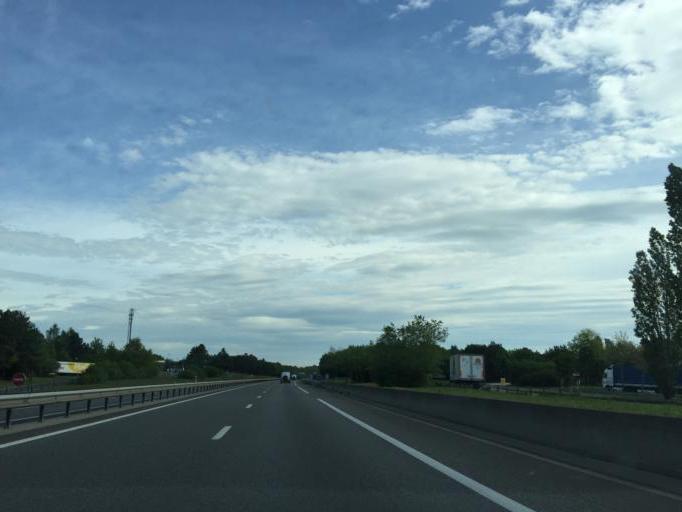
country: FR
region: Rhone-Alpes
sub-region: Departement de la Loire
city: Montrond-les-Bains
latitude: 45.6796
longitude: 4.1558
